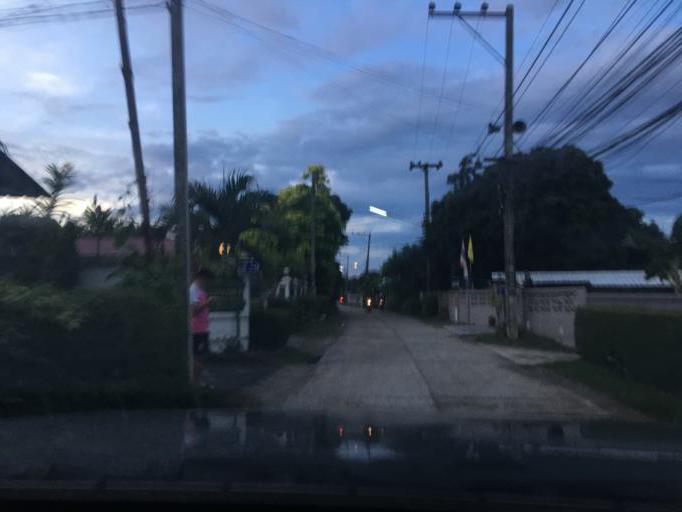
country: TH
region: Chiang Mai
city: San Sai
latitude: 18.8768
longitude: 98.9698
